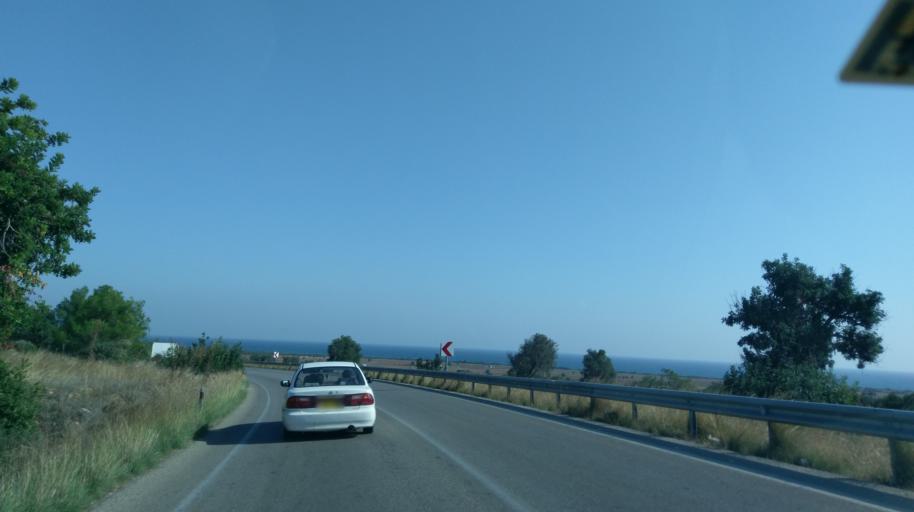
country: CY
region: Ammochostos
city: Leonarisso
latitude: 35.4015
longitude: 34.1026
